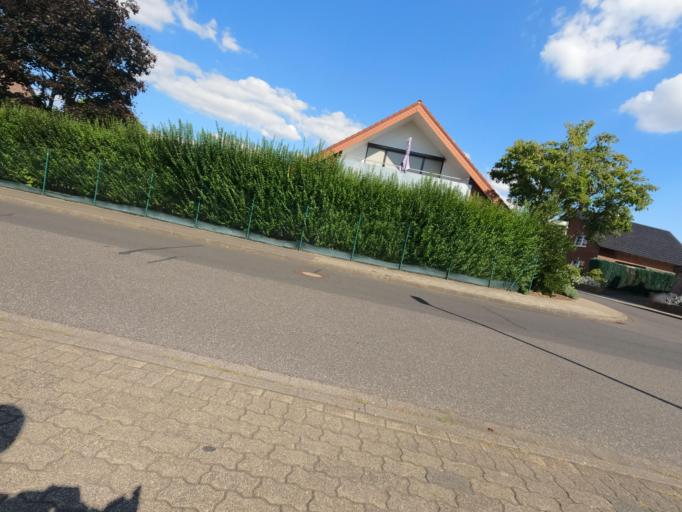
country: DE
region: North Rhine-Westphalia
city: Huckelhoven
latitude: 51.0946
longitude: 6.2075
